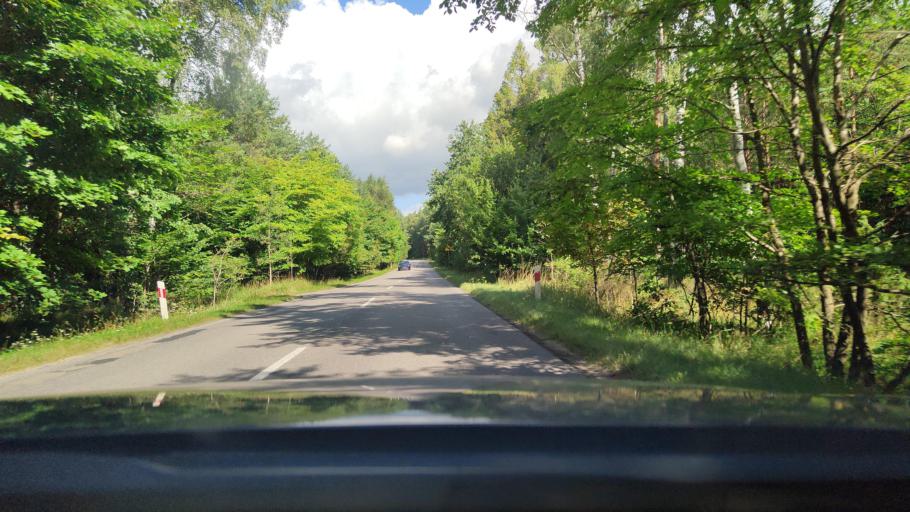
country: PL
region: Pomeranian Voivodeship
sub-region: Powiat wejherowski
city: Wejherowo
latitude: 54.6413
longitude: 18.2191
